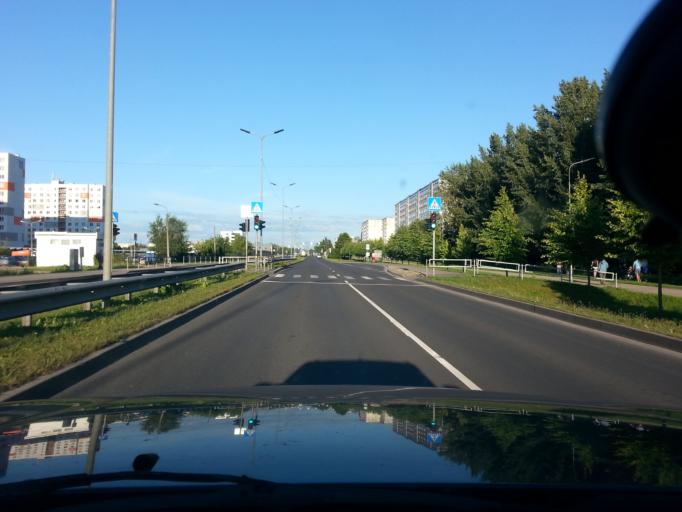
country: LV
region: Stopini
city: Ulbroka
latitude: 56.9456
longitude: 24.2119
